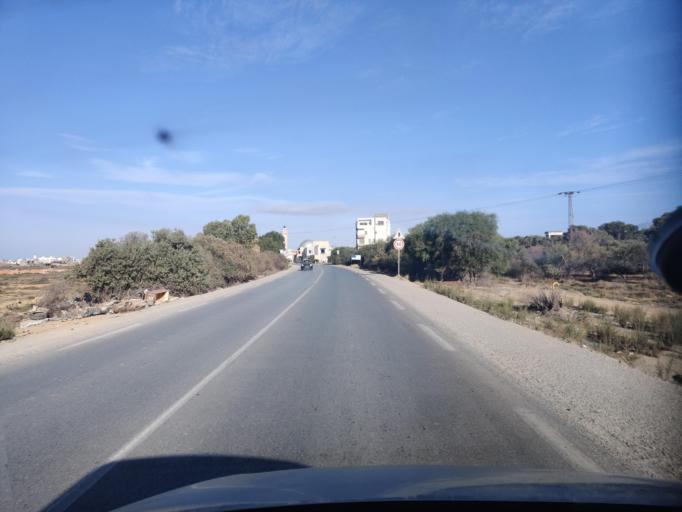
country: TN
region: Ariana
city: Ariana
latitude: 36.9530
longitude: 10.2335
